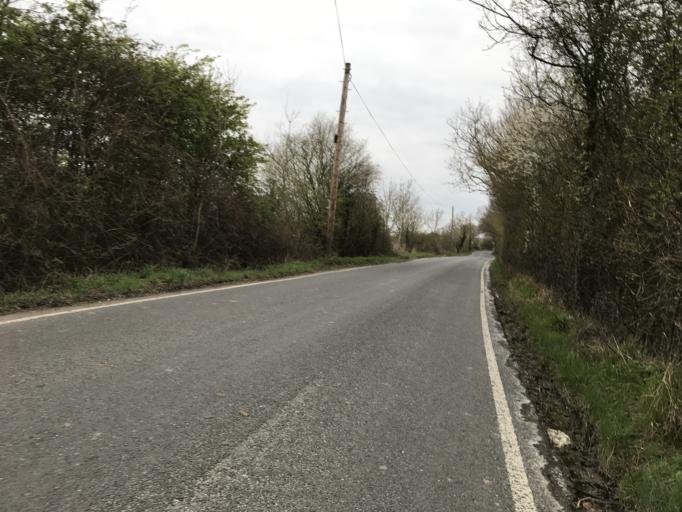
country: GB
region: England
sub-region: Essex
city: Stock
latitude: 51.6735
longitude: 0.4836
